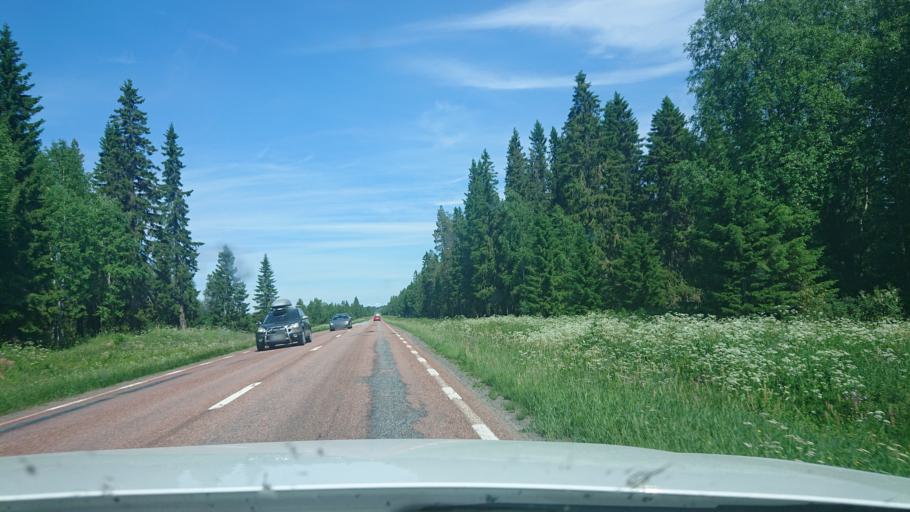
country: SE
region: Jaemtland
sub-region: Stroemsunds Kommun
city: Stroemsund
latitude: 63.7869
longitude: 15.5114
